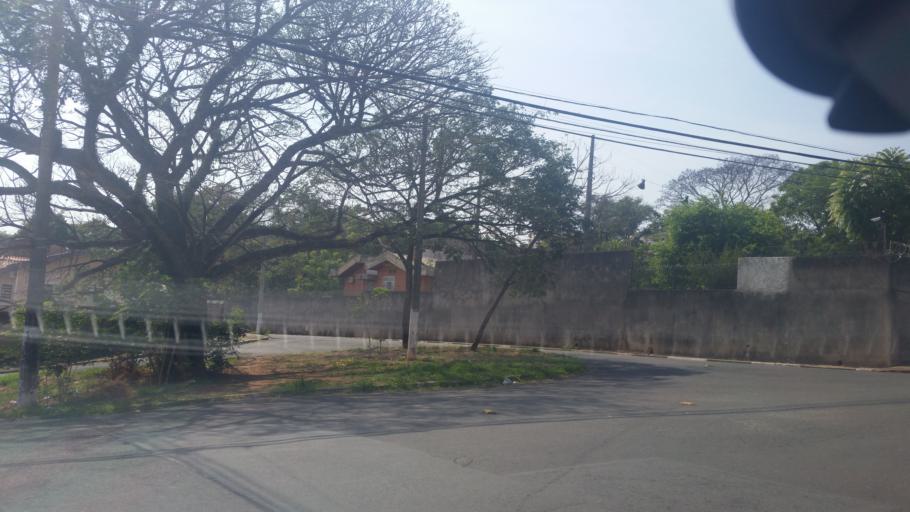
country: BR
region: Sao Paulo
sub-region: Campinas
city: Campinas
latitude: -22.8562
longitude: -47.0370
